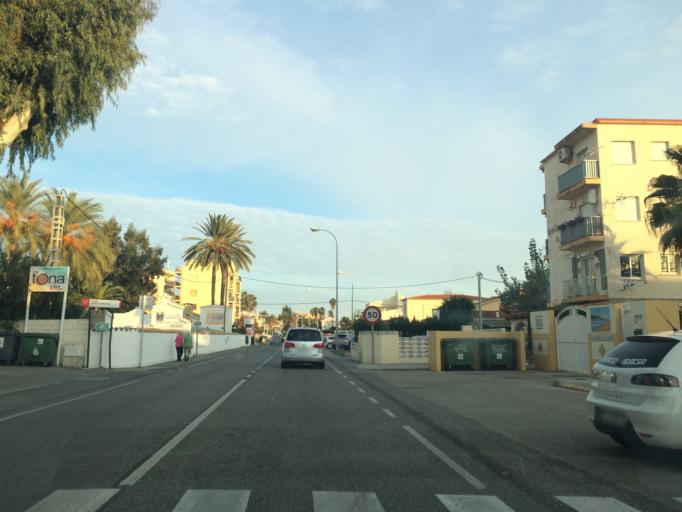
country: ES
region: Valencia
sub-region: Provincia de Alicante
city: Denia
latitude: 38.8563
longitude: 0.0712
